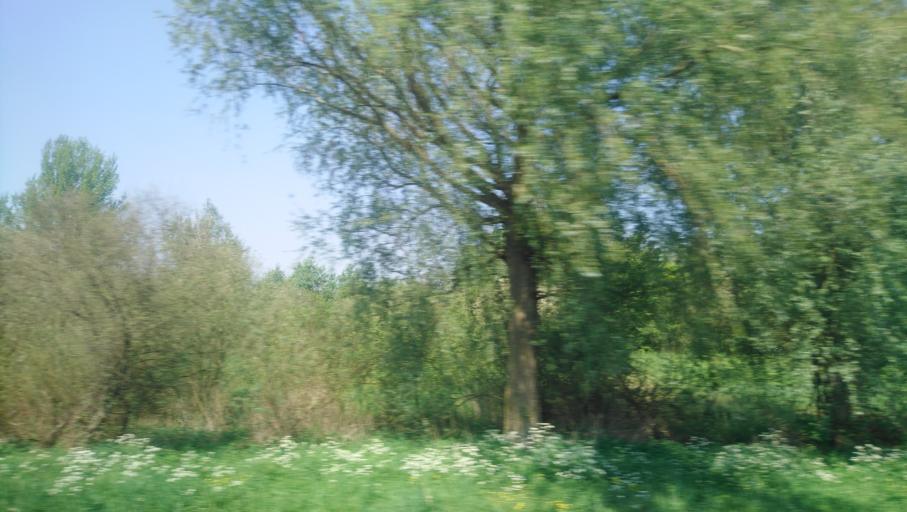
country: NL
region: North Holland
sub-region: Gemeente Zaanstad
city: Zaandam
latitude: 52.3847
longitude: 4.7860
